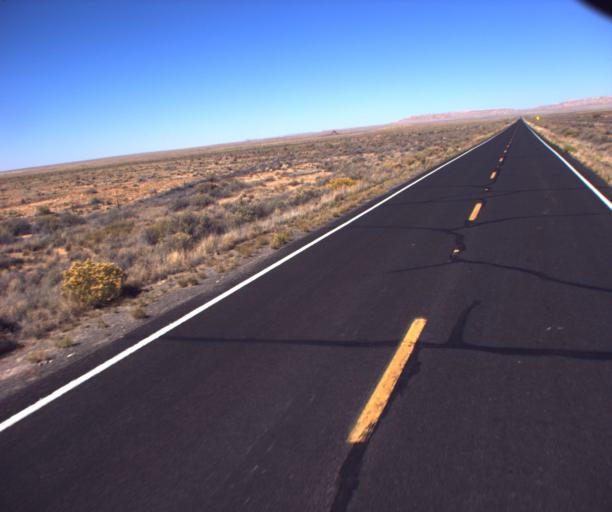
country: US
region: Arizona
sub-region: Navajo County
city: First Mesa
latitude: 35.6852
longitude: -110.5020
